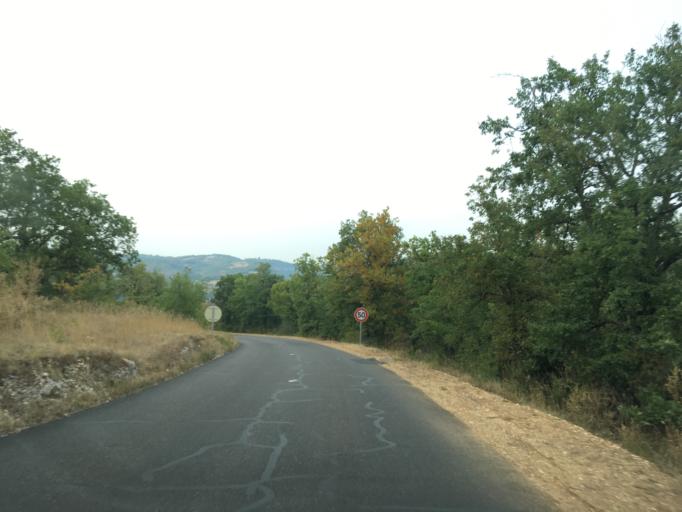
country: FR
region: Midi-Pyrenees
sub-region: Departement du Lot
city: Souillac
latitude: 44.8389
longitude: 1.5593
